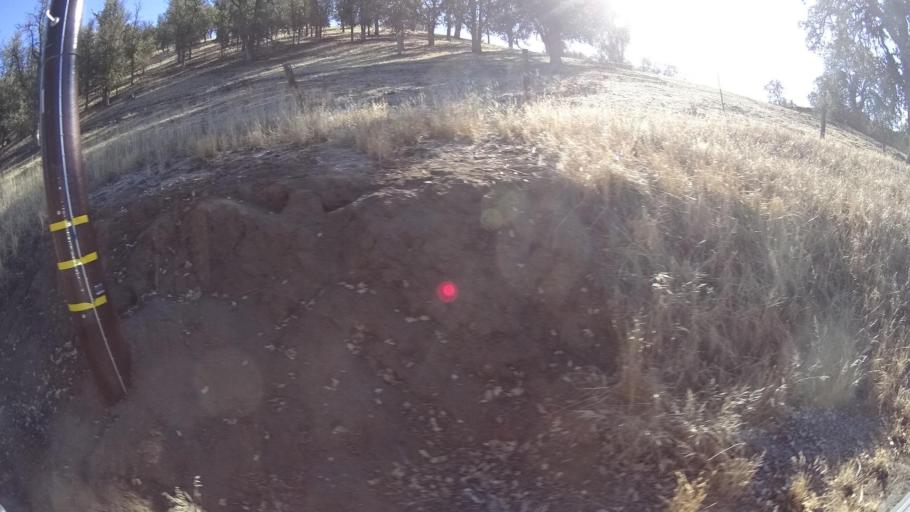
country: US
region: California
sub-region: Kern County
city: Alta Sierra
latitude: 35.7363
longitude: -118.7195
